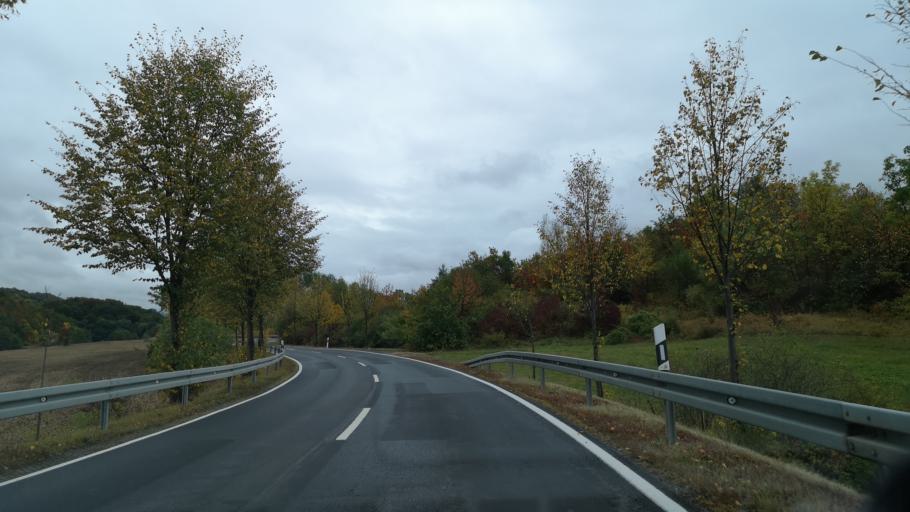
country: DE
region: Thuringia
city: Ifta
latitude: 51.0751
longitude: 10.1543
